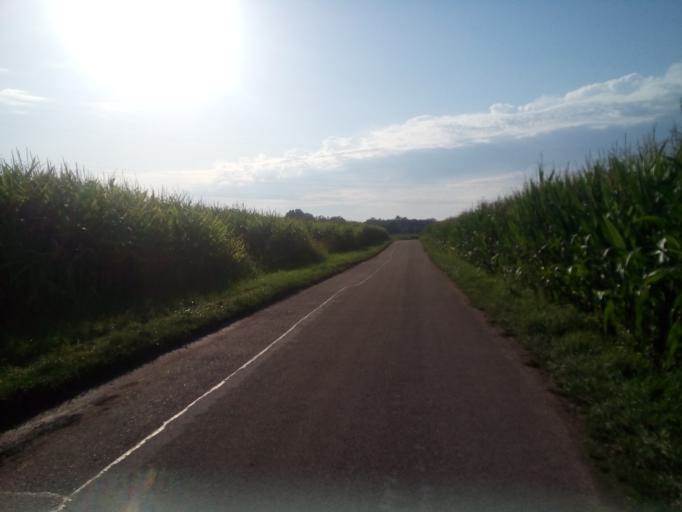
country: DE
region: Baden-Wuerttemberg
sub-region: Karlsruhe Region
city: Lichtenau
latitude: 48.7128
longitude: 7.9850
